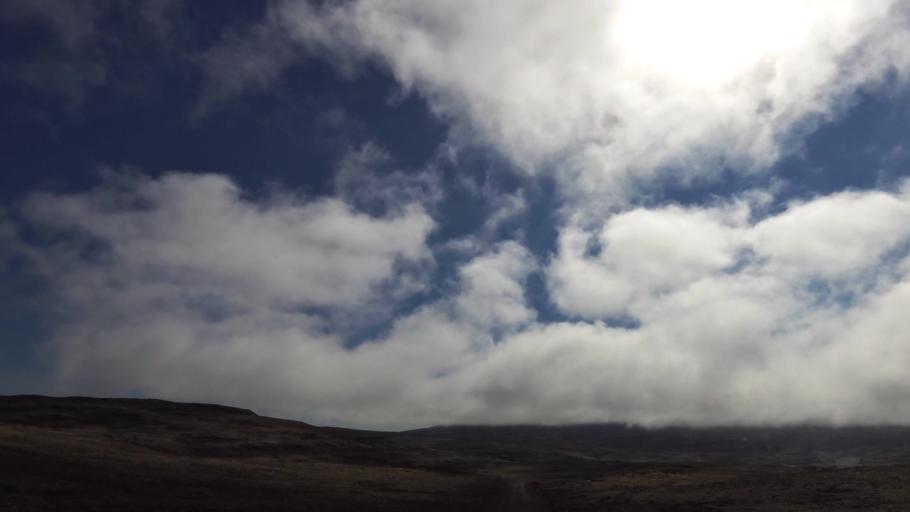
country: IS
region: West
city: Olafsvik
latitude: 65.5541
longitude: -24.2607
